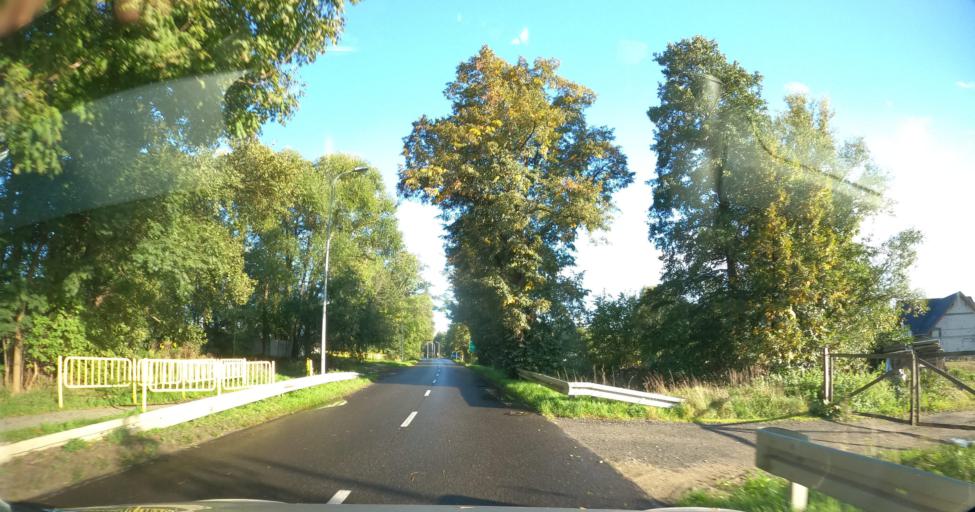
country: PL
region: Lubusz
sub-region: Powiat zielonogorski
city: Zabor
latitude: 51.9292
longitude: 15.6266
